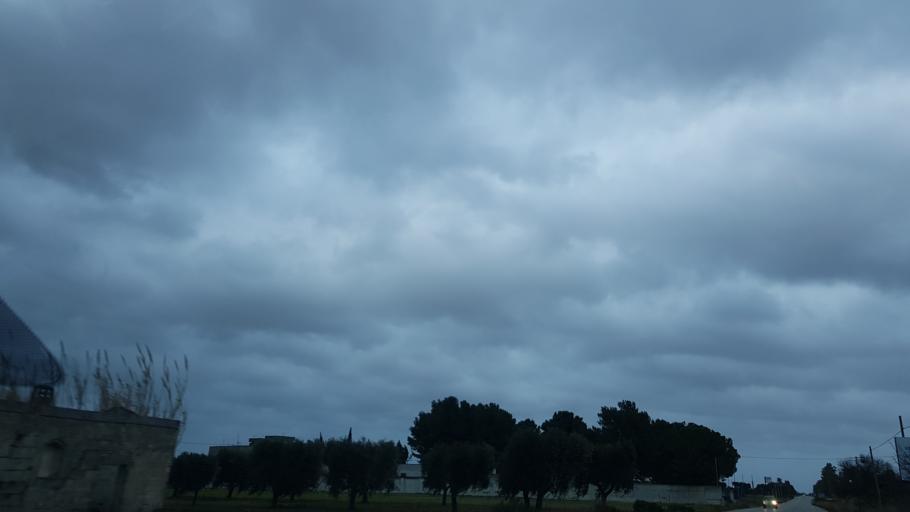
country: IT
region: Apulia
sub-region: Provincia di Brindisi
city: Mesagne
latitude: 40.6507
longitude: 17.8265
